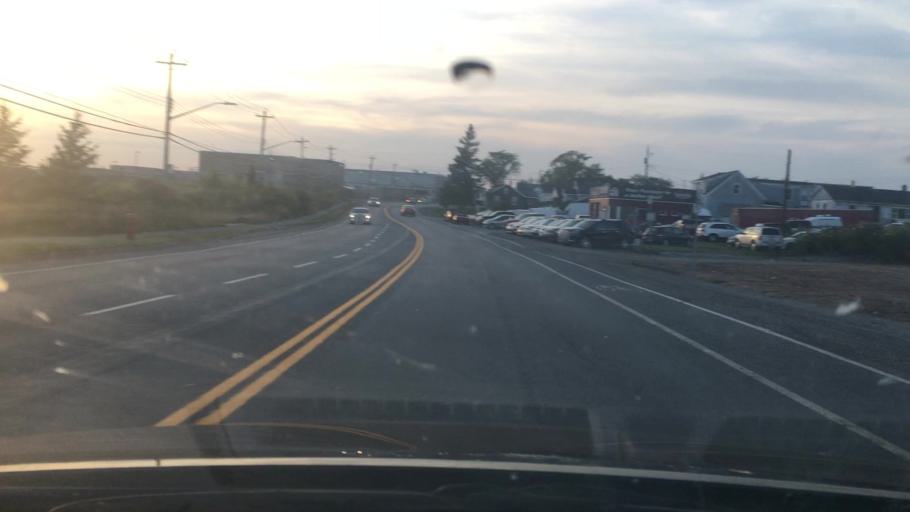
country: CA
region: Nova Scotia
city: Cole Harbour
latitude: 44.6239
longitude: -63.5109
